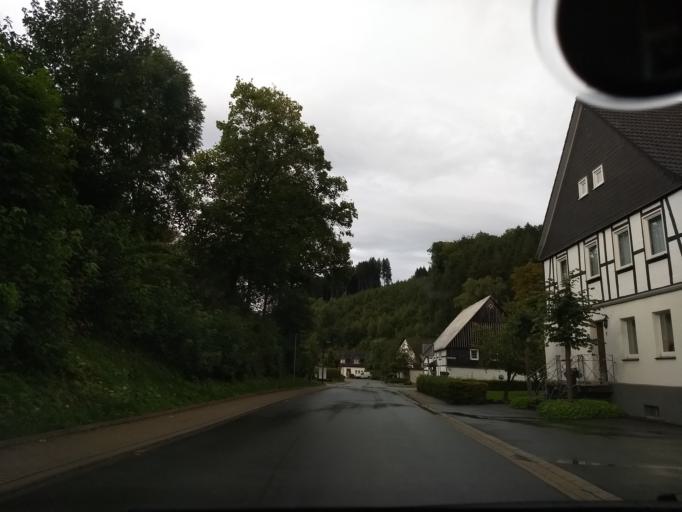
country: DE
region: North Rhine-Westphalia
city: Eslohe
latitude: 51.2298
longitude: 8.1343
